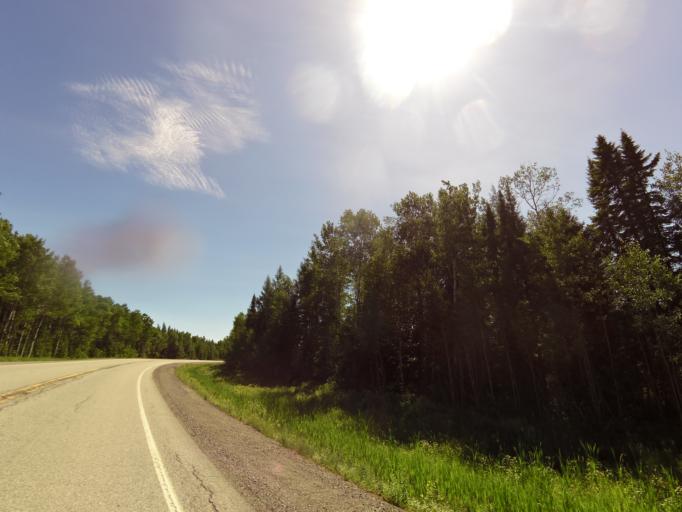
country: CA
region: Quebec
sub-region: Nord-du-Quebec
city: Lebel-sur-Quevillon
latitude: 48.8373
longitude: -77.1105
